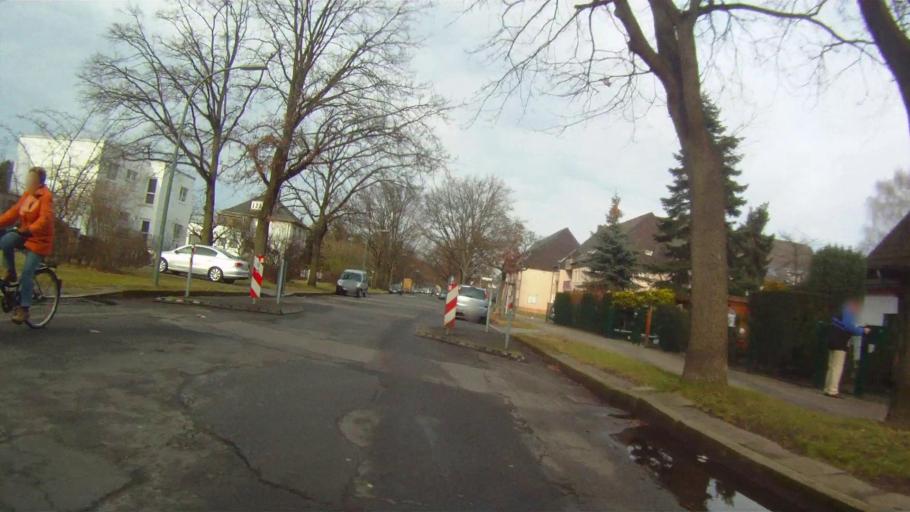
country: DE
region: Berlin
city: Rudow
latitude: 52.4243
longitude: 13.4911
